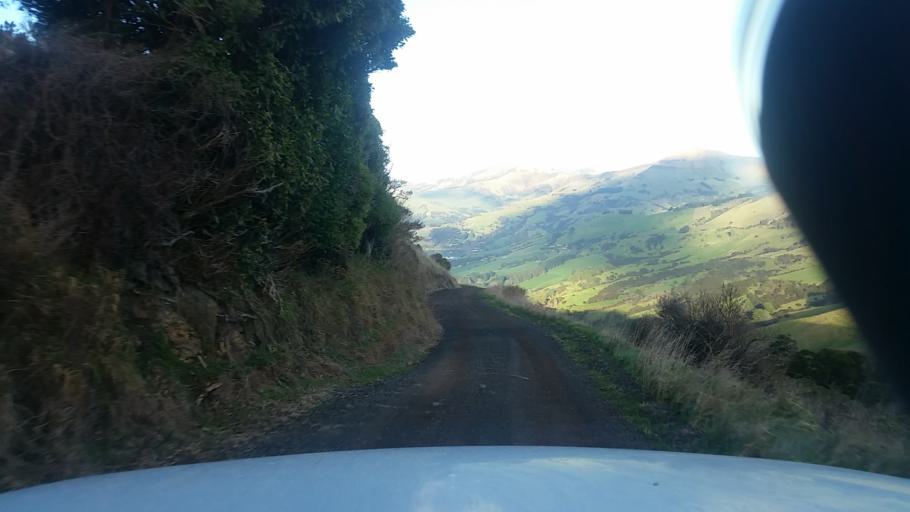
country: NZ
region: Canterbury
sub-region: Christchurch City
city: Christchurch
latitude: -43.7217
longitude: 172.9554
